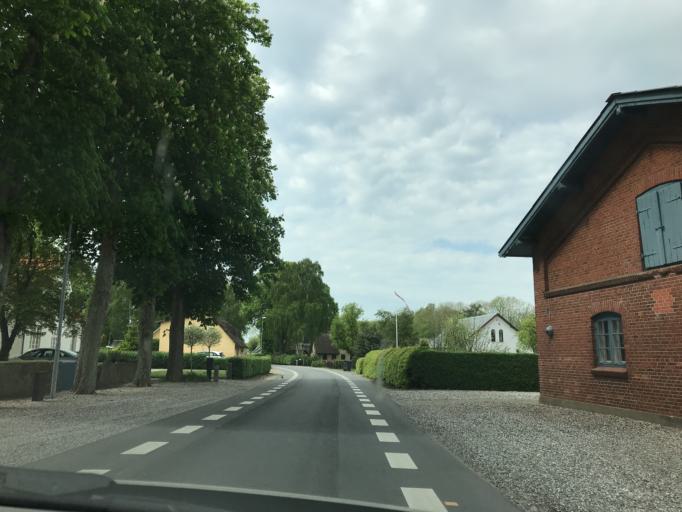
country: DK
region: South Denmark
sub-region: Assens Kommune
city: Assens
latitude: 55.3275
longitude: 9.9281
